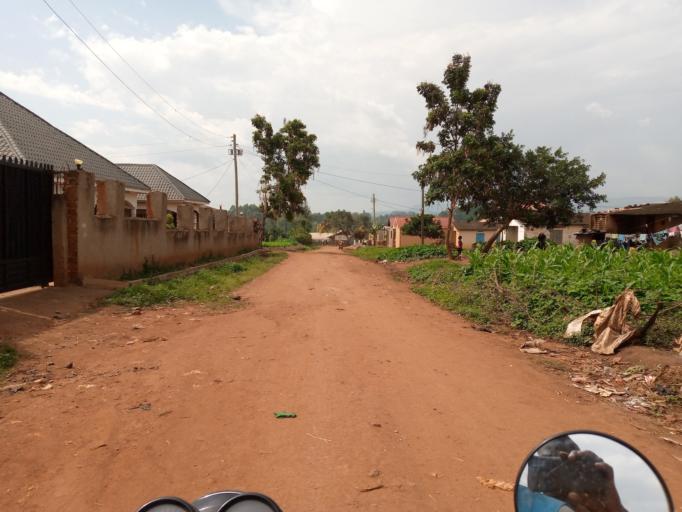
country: UG
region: Eastern Region
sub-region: Mbale District
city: Mbale
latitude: 1.0837
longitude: 34.1593
